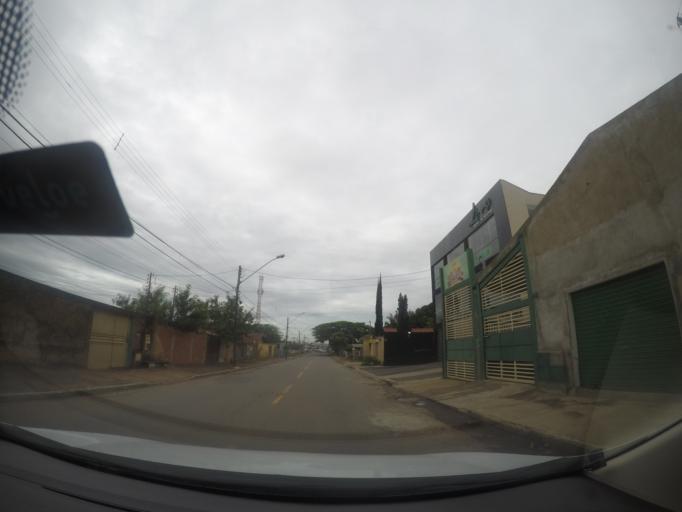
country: BR
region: Goias
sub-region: Goiania
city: Goiania
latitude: -16.6545
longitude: -49.3161
